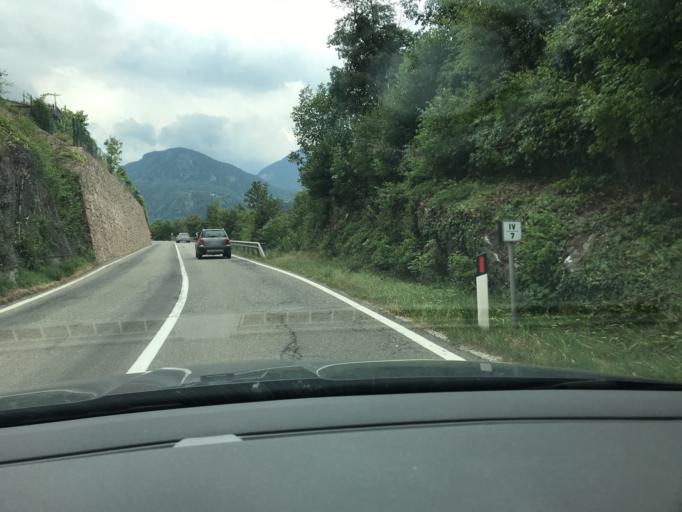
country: IT
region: Trentino-Alto Adige
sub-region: Bolzano
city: Laion
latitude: 46.6021
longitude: 11.5529
